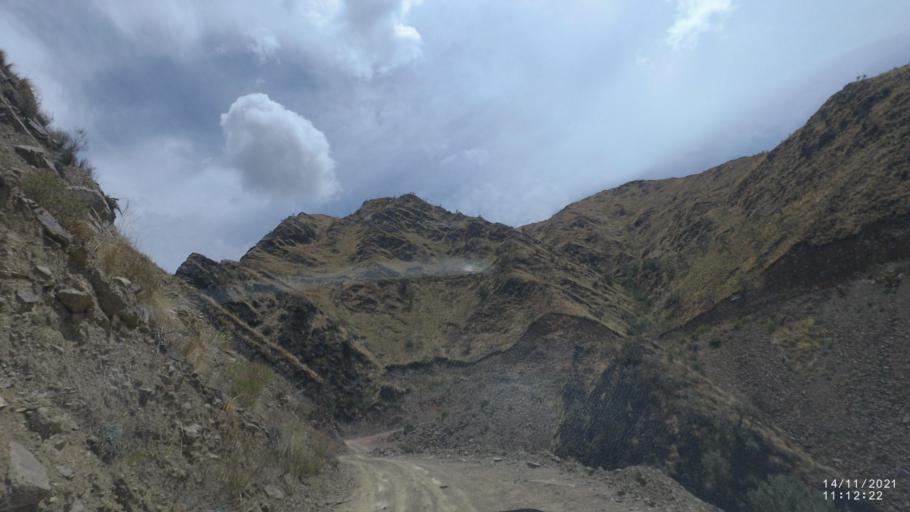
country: BO
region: Cochabamba
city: Cochabamba
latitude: -17.3270
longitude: -66.0502
